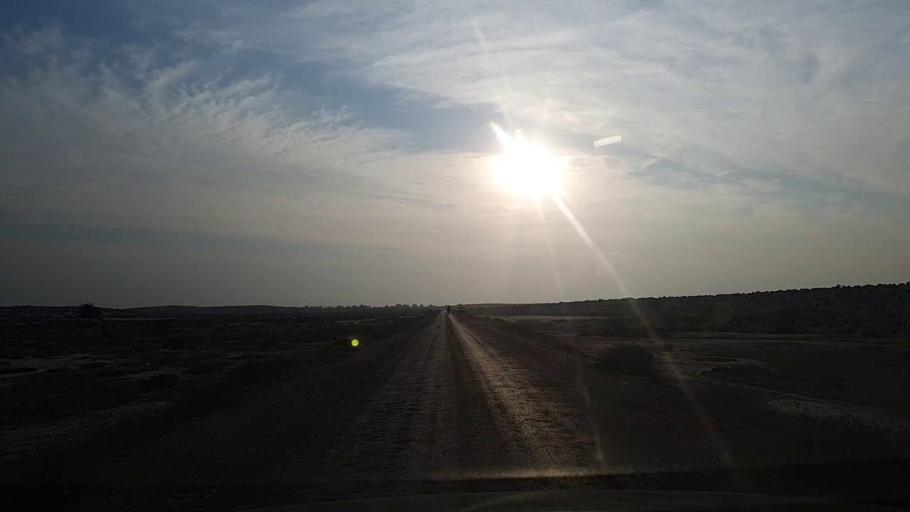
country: PK
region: Sindh
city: Jam Sahib
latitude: 26.4163
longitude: 68.5181
